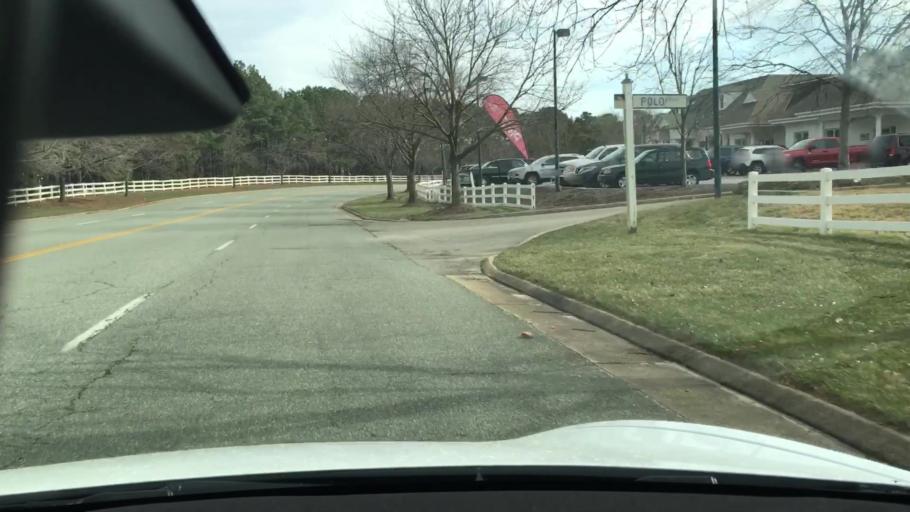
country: US
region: Virginia
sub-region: Chesterfield County
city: Bon Air
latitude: 37.5272
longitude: -77.6100
